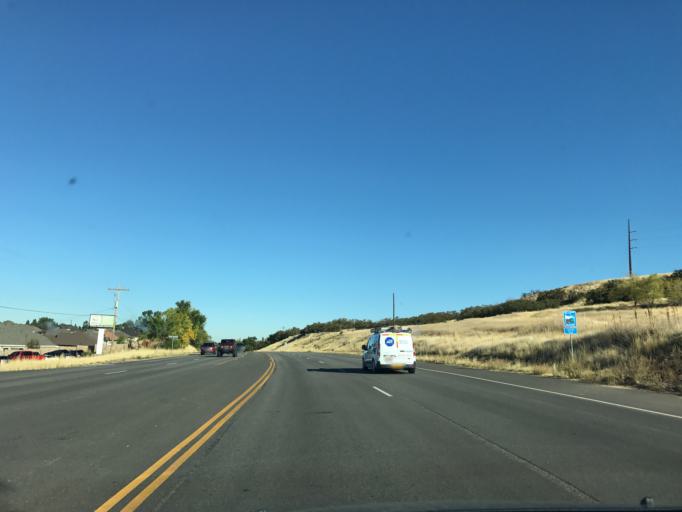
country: US
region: Utah
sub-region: Weber County
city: Uintah
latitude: 41.1624
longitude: -111.9406
